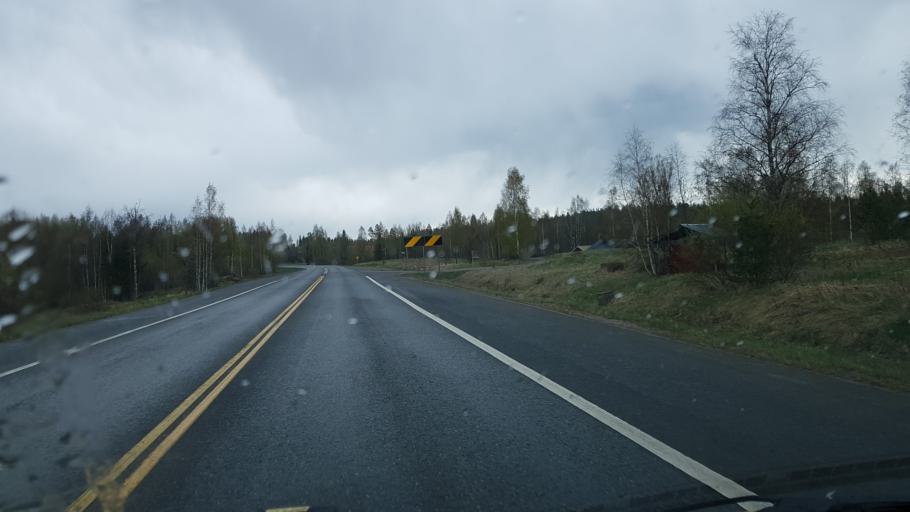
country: FI
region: Pirkanmaa
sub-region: Tampere
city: Pirkkala
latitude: 61.4224
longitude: 23.6346
